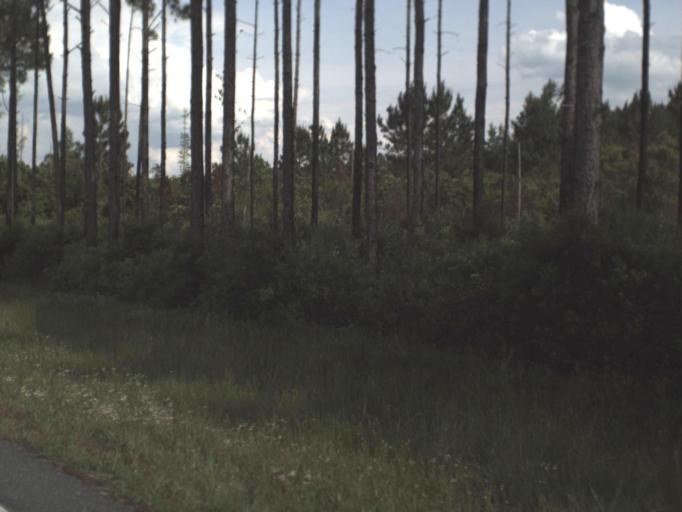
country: US
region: Florida
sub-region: Baker County
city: Macclenny
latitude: 30.5670
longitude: -82.4147
